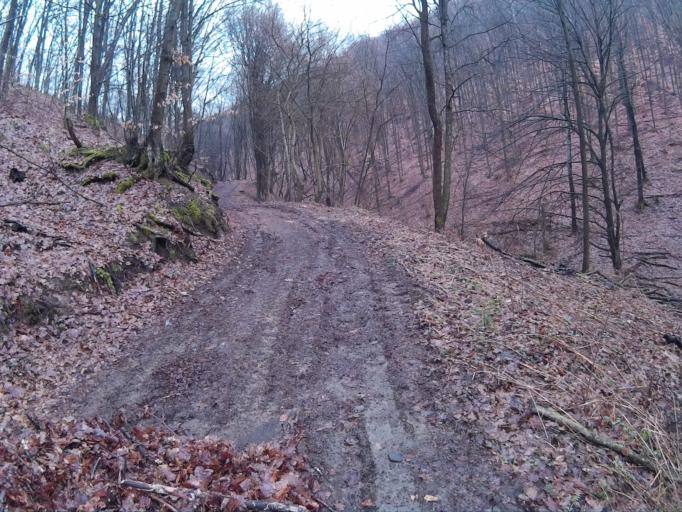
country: HU
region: Borsod-Abauj-Zemplen
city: Sarospatak
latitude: 48.4209
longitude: 21.5492
